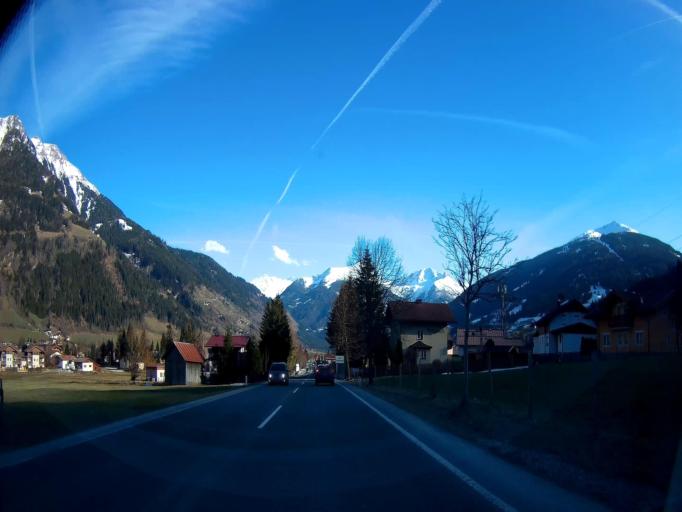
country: AT
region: Salzburg
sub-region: Politischer Bezirk Sankt Johann im Pongau
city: Bad Hofgastein
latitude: 47.1609
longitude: 13.1028
